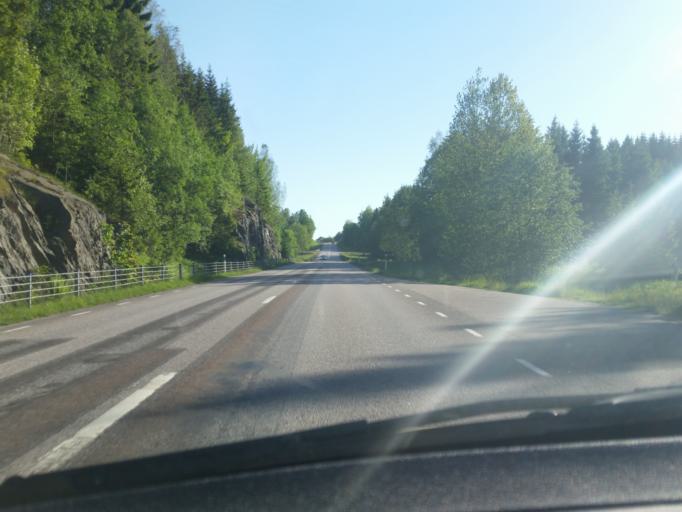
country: SE
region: Vaestra Goetaland
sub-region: Fargelanda Kommun
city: Faergelanda
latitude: 58.5794
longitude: 12.0166
